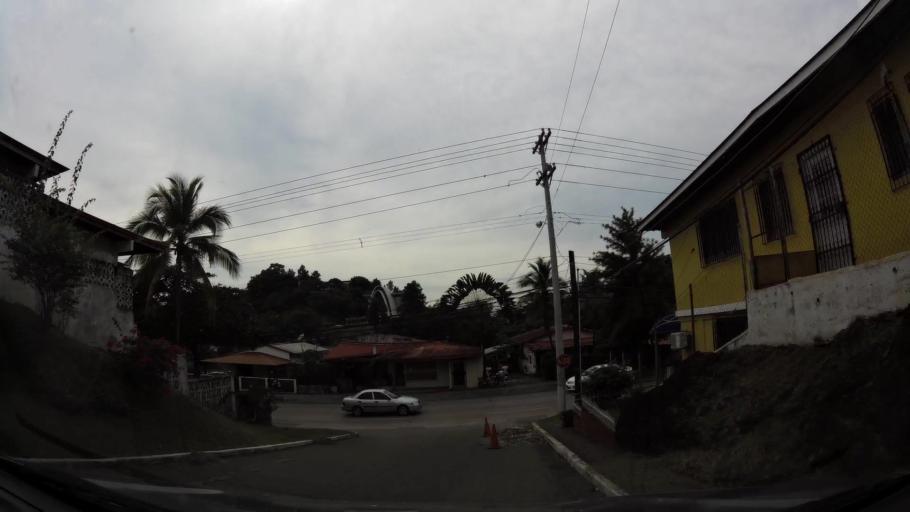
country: PA
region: Panama
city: Panama
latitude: 9.0224
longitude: -79.5177
